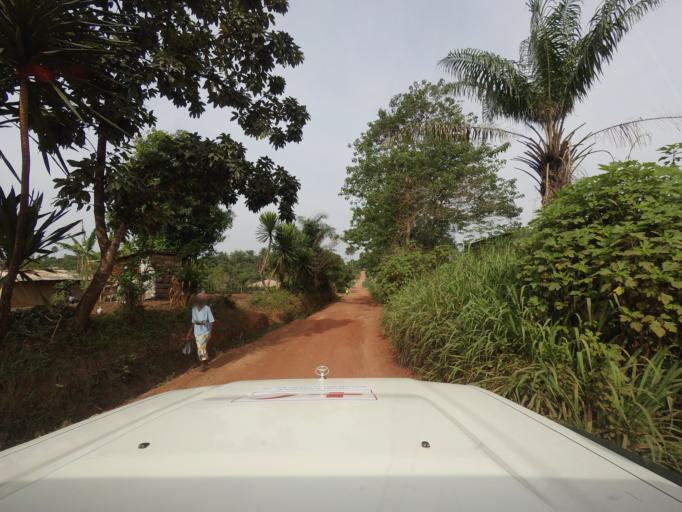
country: GN
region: Nzerekore
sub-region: Macenta
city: Macenta
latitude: 8.5401
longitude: -9.4867
